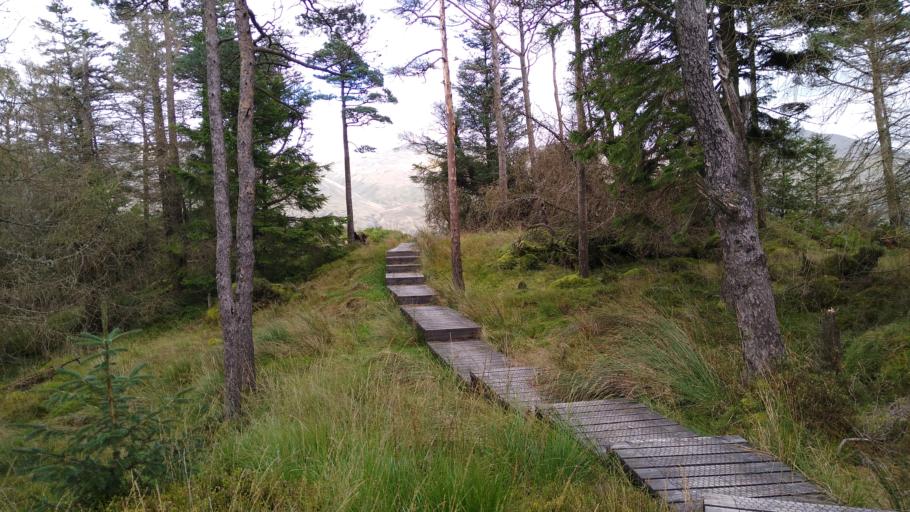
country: GB
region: England
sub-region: Cumbria
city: Keswick
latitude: 54.5593
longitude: -3.0795
